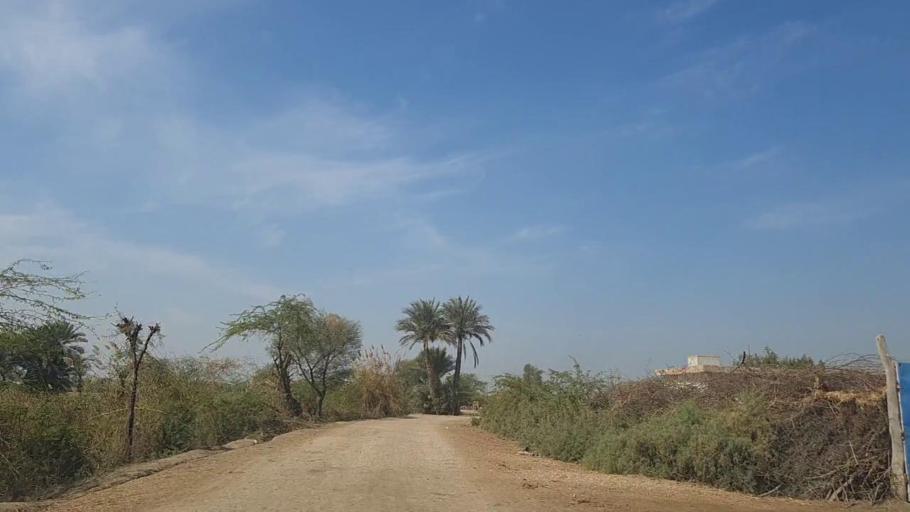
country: PK
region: Sindh
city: Mirpur Khas
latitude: 25.4811
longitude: 68.9670
